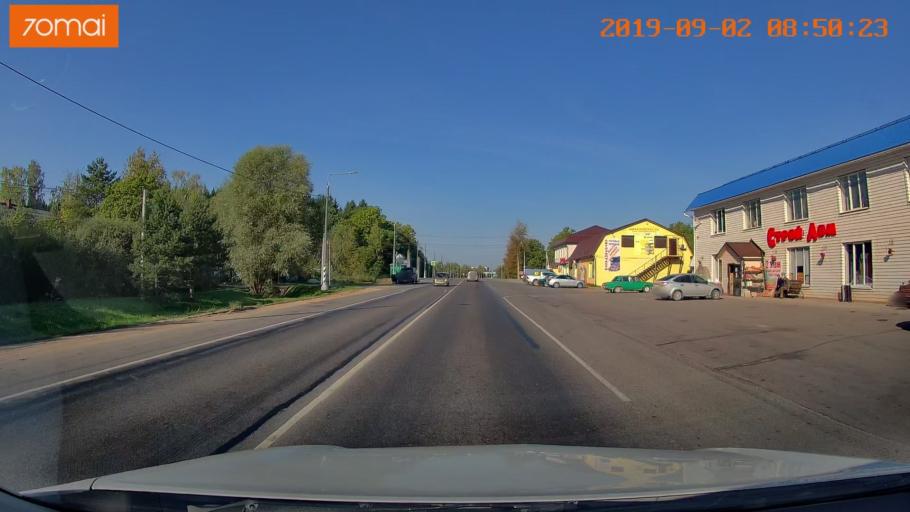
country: RU
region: Kaluga
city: Medyn'
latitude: 54.9654
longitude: 35.8867
